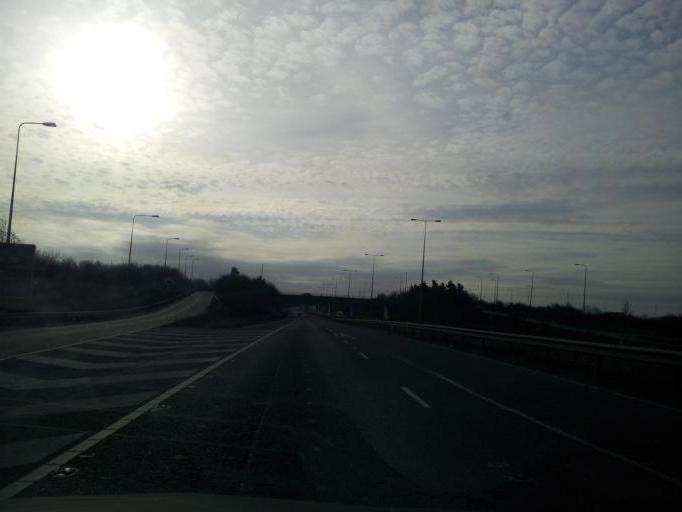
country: GB
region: England
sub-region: Peterborough
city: Castor
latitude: 52.5363
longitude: -0.3214
